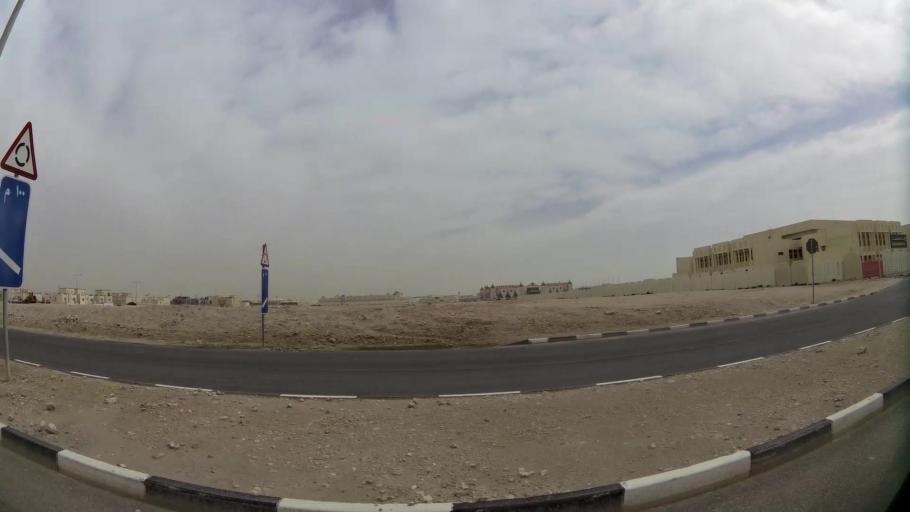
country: QA
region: Baladiyat ad Dawhah
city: Doha
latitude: 25.2160
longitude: 51.4919
